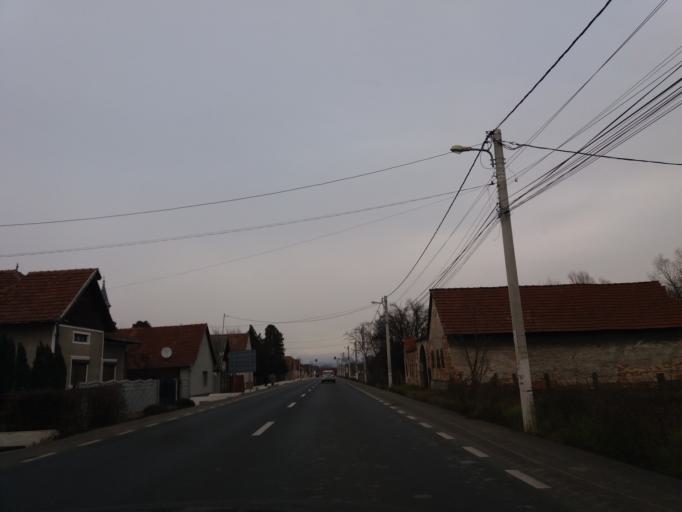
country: RO
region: Hunedoara
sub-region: Comuna Bacia
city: Bacia
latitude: 45.7818
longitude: 23.0010
